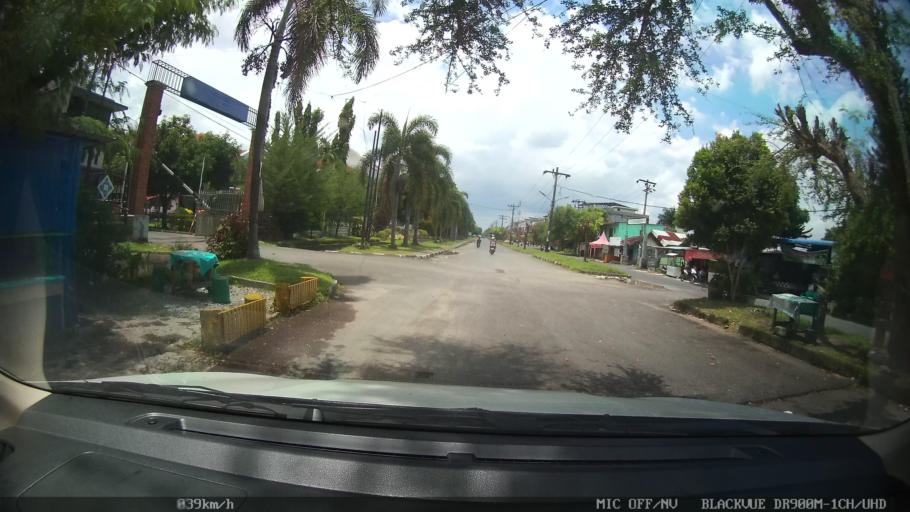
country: ID
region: North Sumatra
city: Medan
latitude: 3.6139
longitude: 98.7188
